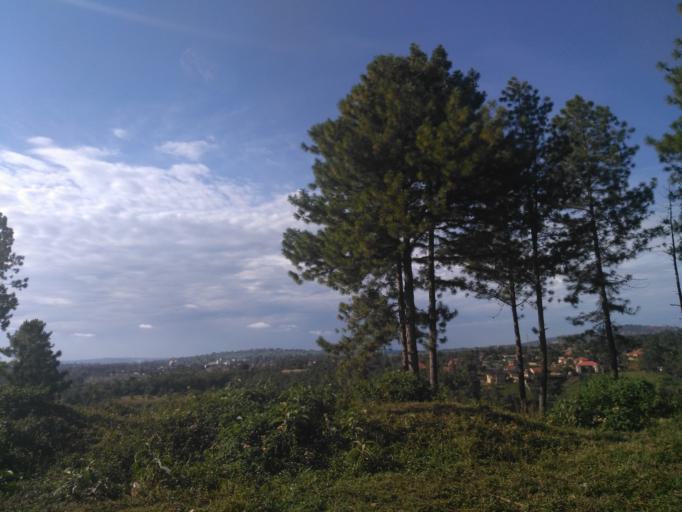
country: UG
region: Eastern Region
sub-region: Jinja District
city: Jinja
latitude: 0.4571
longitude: 33.1803
